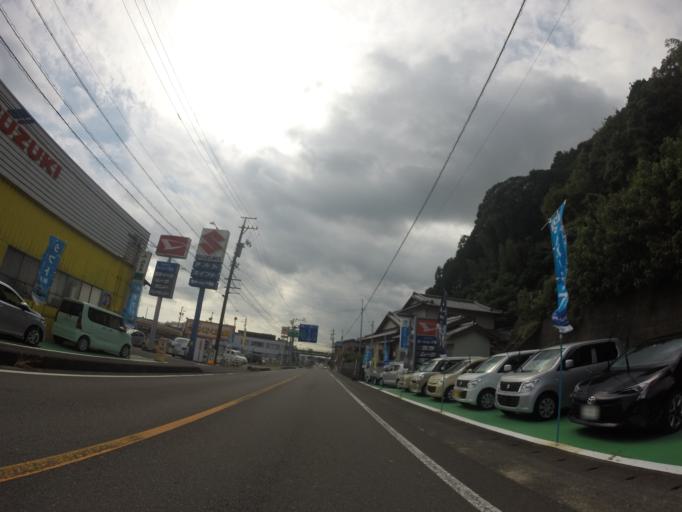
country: JP
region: Shizuoka
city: Shimada
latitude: 34.8494
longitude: 138.1829
